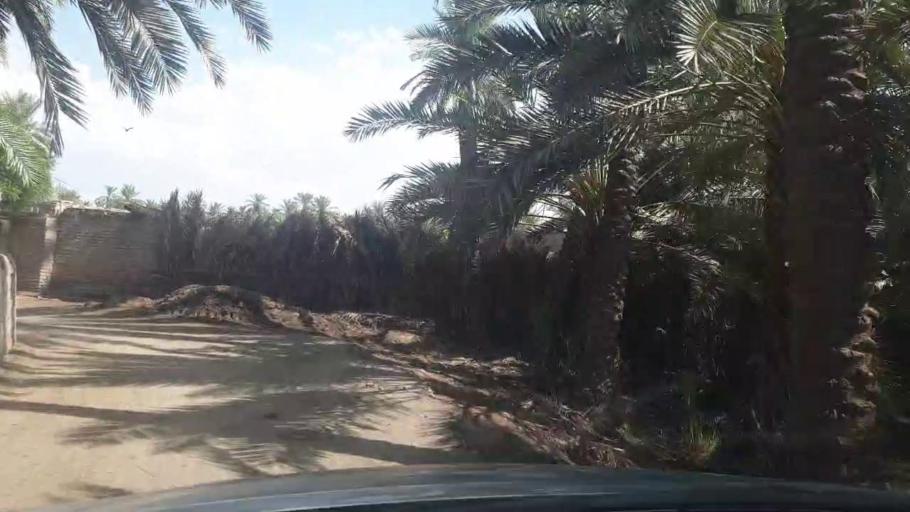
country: PK
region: Sindh
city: Khairpur
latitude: 27.5492
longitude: 68.7871
